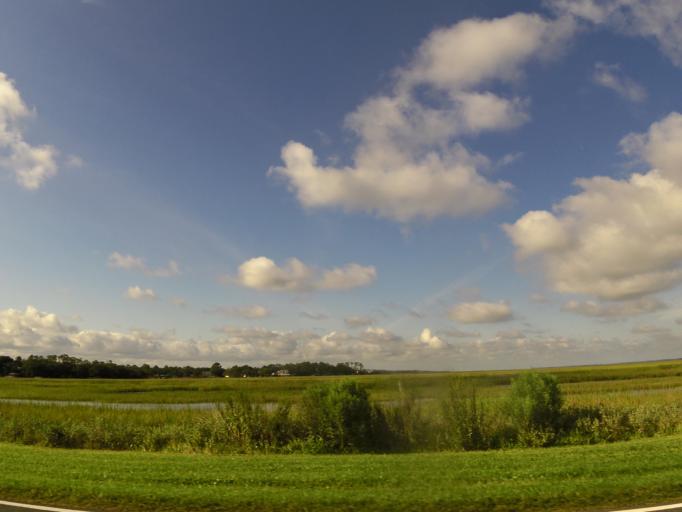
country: US
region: Georgia
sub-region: Glynn County
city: Saint Simons Island
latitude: 31.1817
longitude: -81.3663
